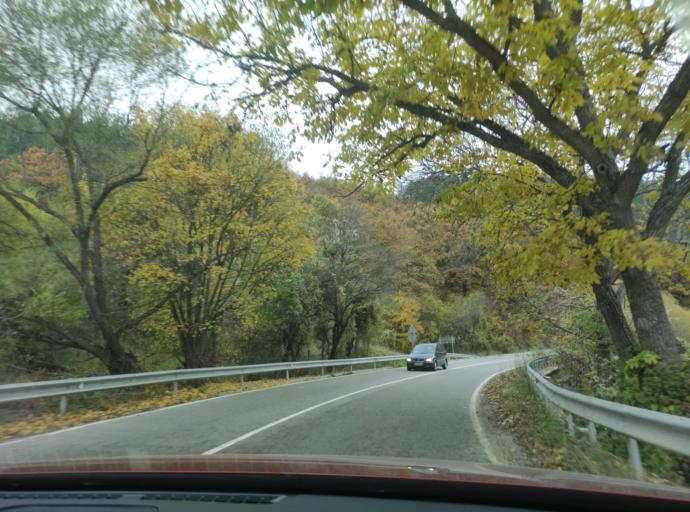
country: BG
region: Sofiya
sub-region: Obshtina Godech
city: Godech
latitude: 42.9758
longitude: 23.1380
